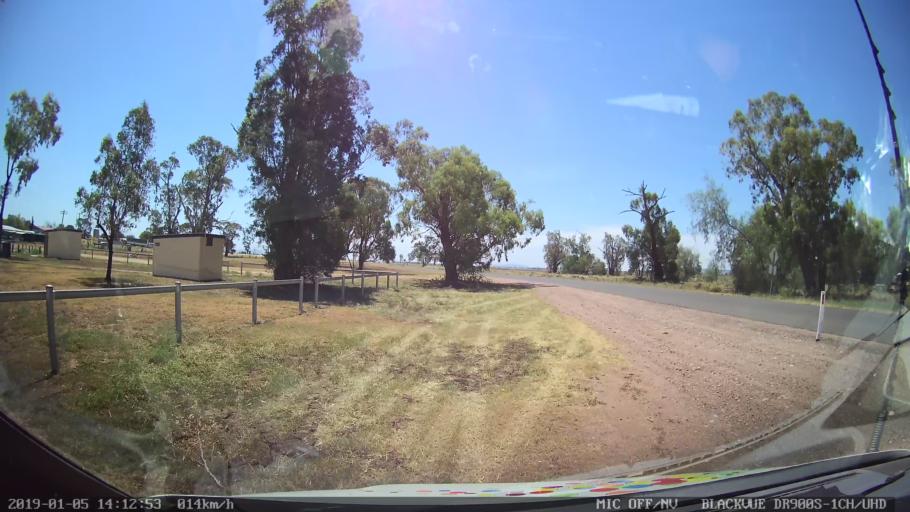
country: AU
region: New South Wales
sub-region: Liverpool Plains
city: Quirindi
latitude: -31.2471
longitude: 150.4684
